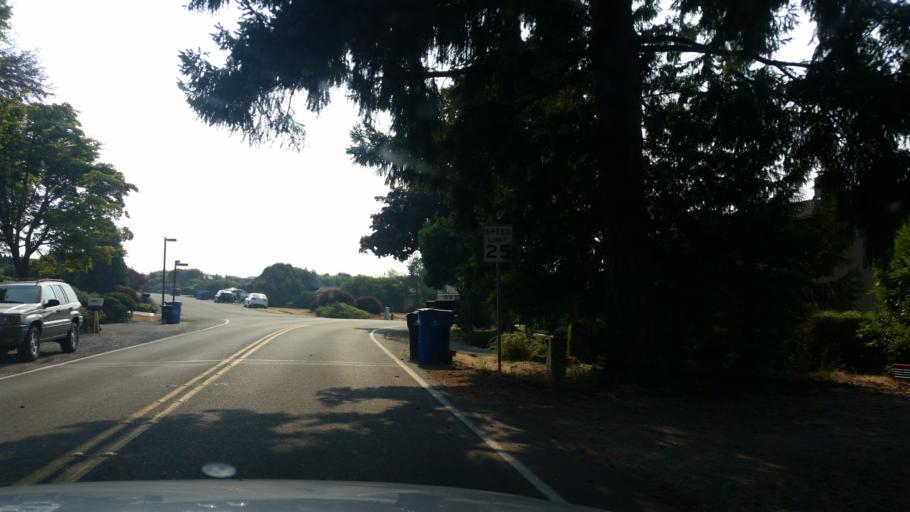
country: US
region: Washington
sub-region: King County
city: Shoreline
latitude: 47.7556
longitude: -122.3705
